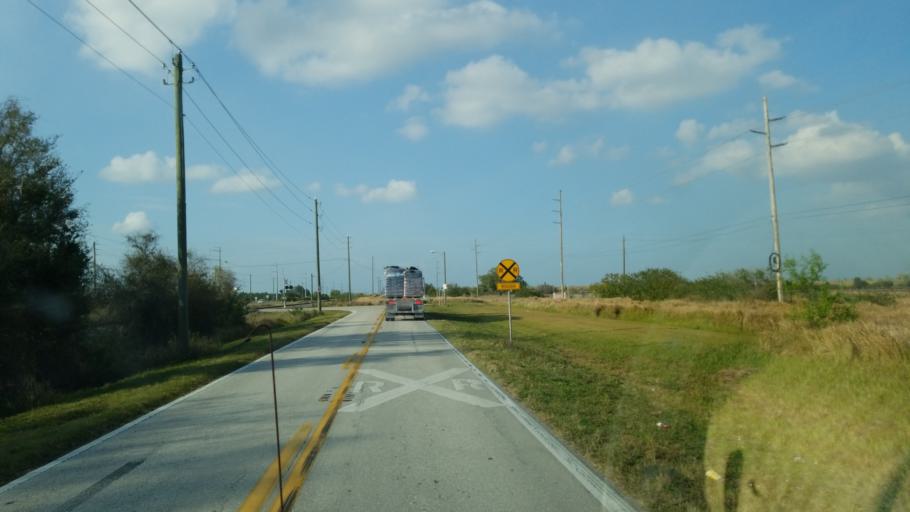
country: US
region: Florida
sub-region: Hardee County
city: Bowling Green
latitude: 27.6976
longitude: -81.9576
